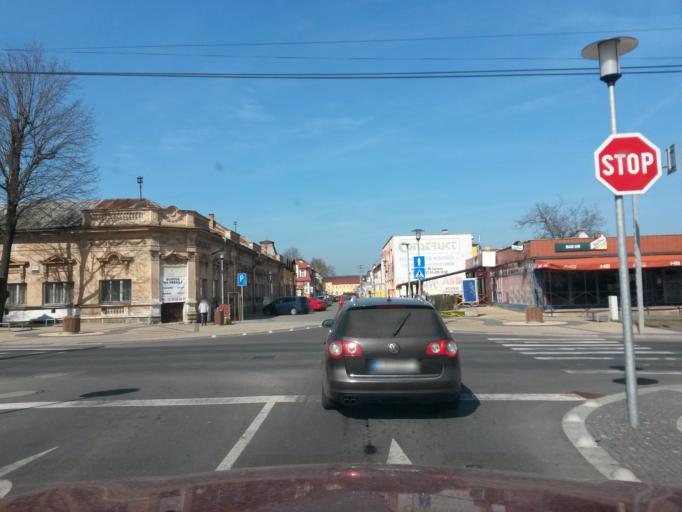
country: SK
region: Banskobystricky
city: Lucenec
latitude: 48.3329
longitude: 19.6664
